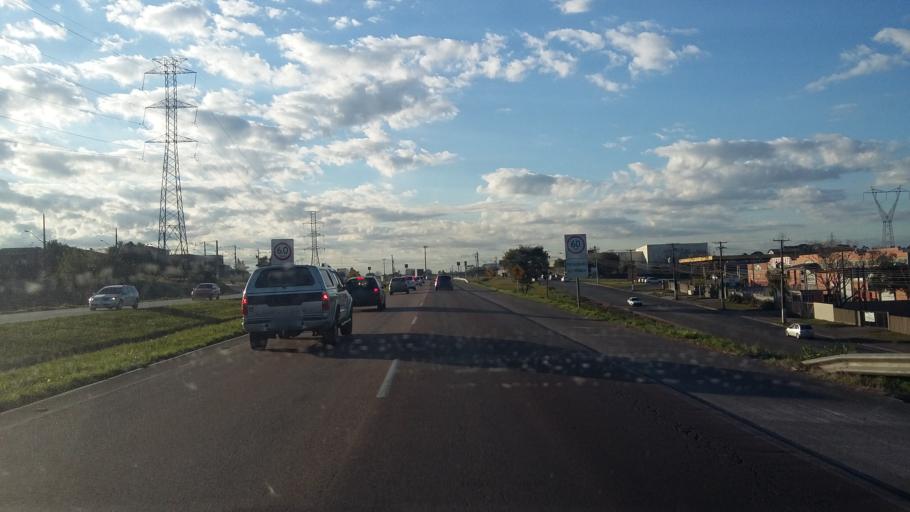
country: BR
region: Parana
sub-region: Curitiba
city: Curitiba
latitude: -25.4980
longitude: -49.3424
